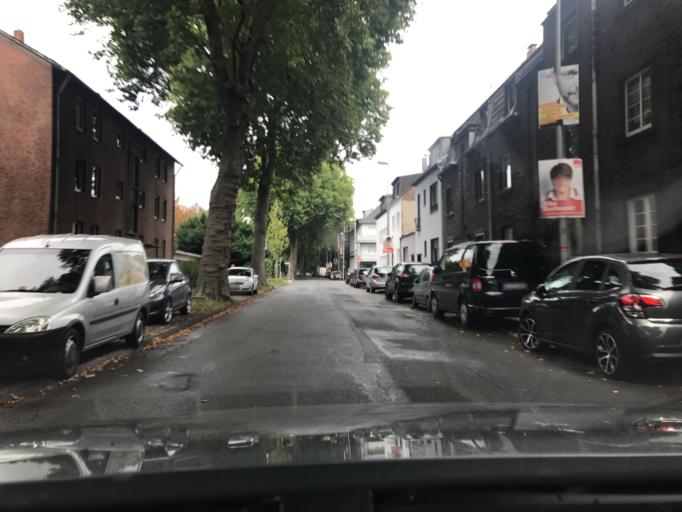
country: DE
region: North Rhine-Westphalia
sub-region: Regierungsbezirk Dusseldorf
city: Krefeld
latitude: 51.3403
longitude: 6.5916
